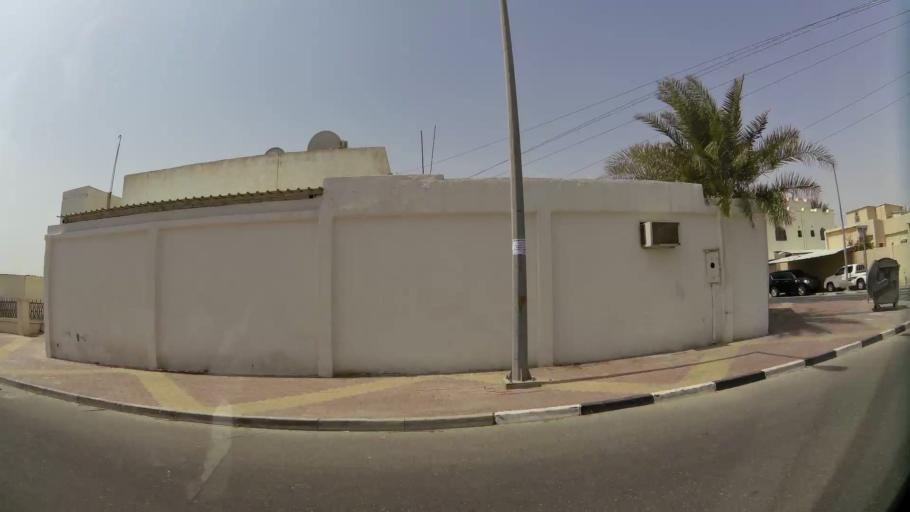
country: QA
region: Baladiyat ad Dawhah
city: Doha
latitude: 25.3156
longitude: 51.4810
